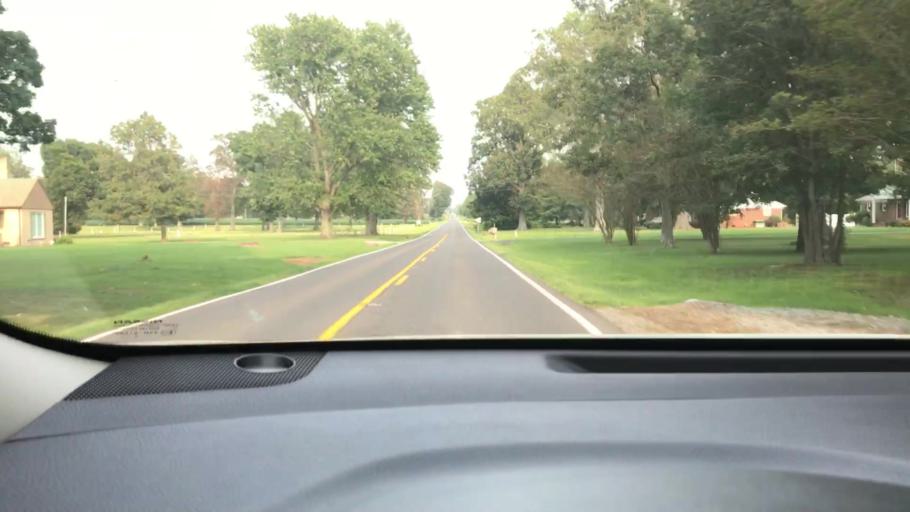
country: US
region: Kentucky
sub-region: Calloway County
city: Murray
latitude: 36.5807
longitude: -88.2705
